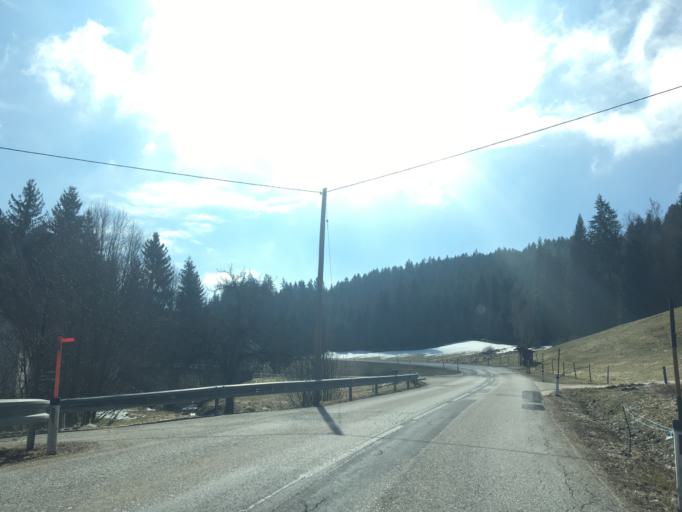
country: AT
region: Upper Austria
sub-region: Politischer Bezirk Perg
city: Sankt Georgen am Walde
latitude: 48.3876
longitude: 14.8892
